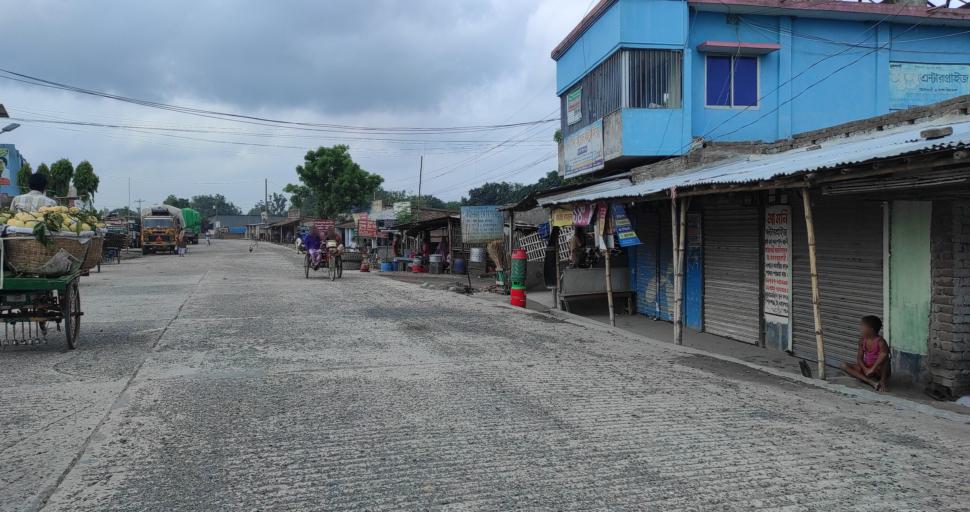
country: BD
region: Rajshahi
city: Shibganj
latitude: 24.8354
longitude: 88.1416
